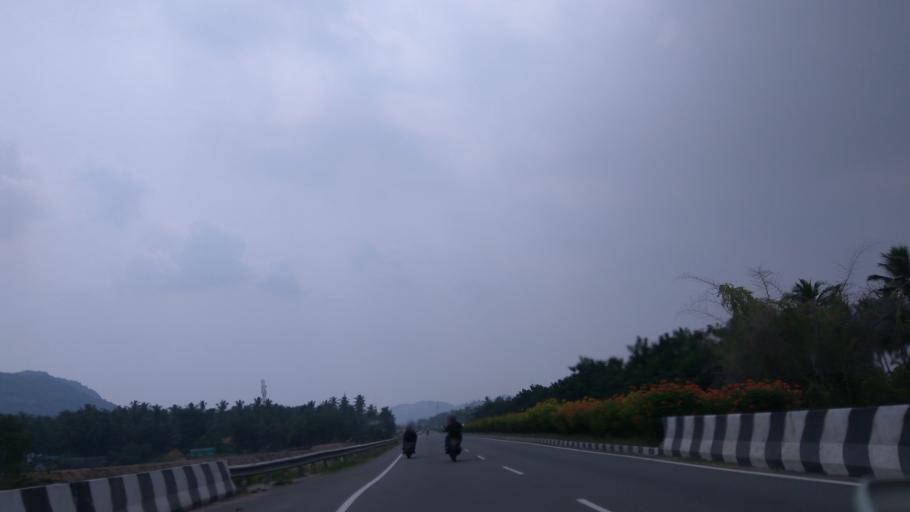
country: IN
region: Tamil Nadu
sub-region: Krishnagiri
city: Kaverippattanam
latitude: 12.3851
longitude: 78.2190
